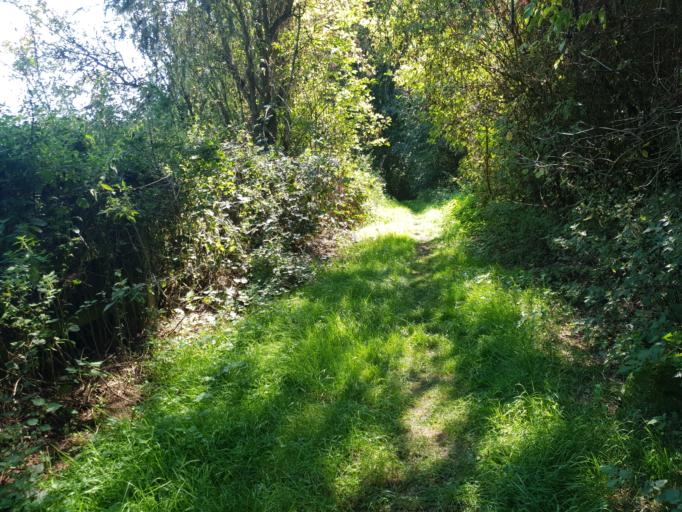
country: GB
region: England
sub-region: Essex
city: Wivenhoe
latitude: 51.9252
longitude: 0.9684
